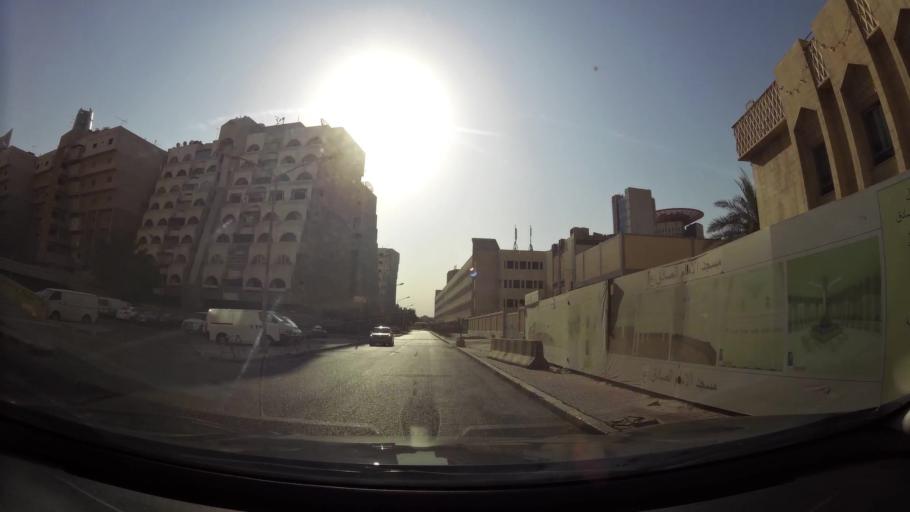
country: KW
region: Al Asimah
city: Kuwait City
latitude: 29.3749
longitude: 47.9803
